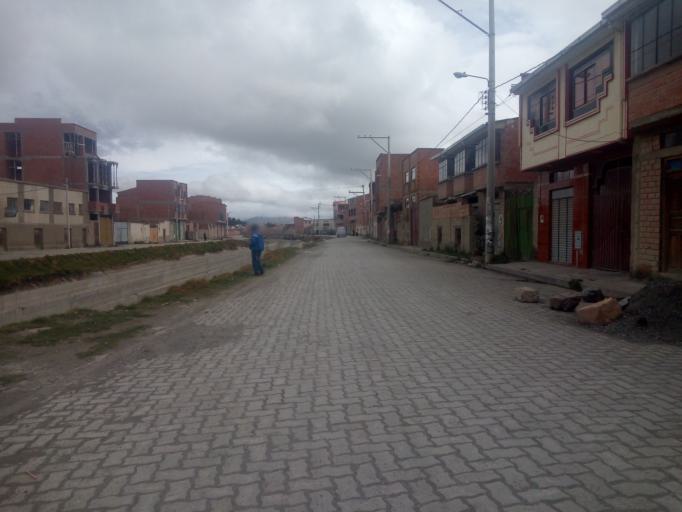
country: BO
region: La Paz
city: Achacachi
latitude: -16.0433
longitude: -68.6872
